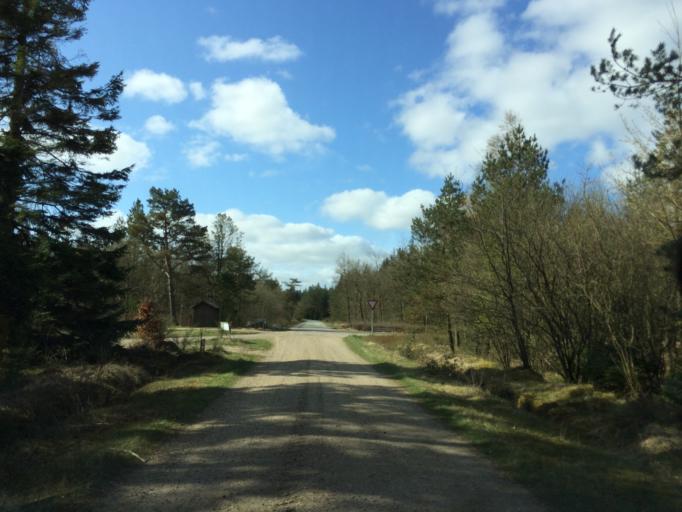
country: DK
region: Central Jutland
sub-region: Holstebro Kommune
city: Ulfborg
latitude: 56.2171
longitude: 8.4585
